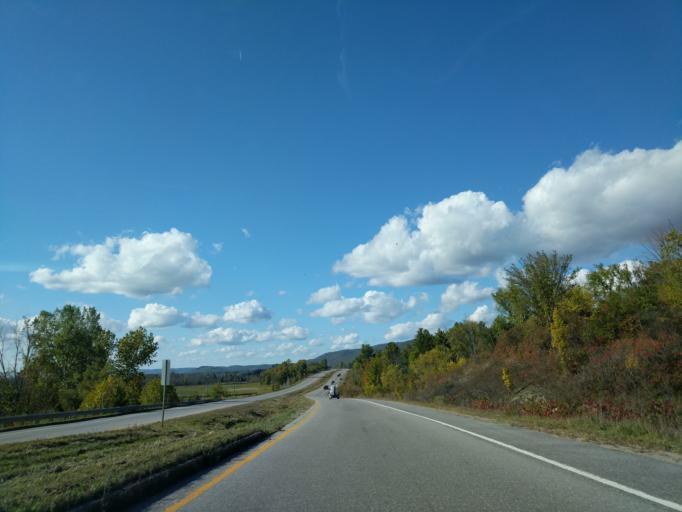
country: CA
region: Quebec
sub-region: Outaouais
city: Wakefield
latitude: 45.5082
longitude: -75.9738
